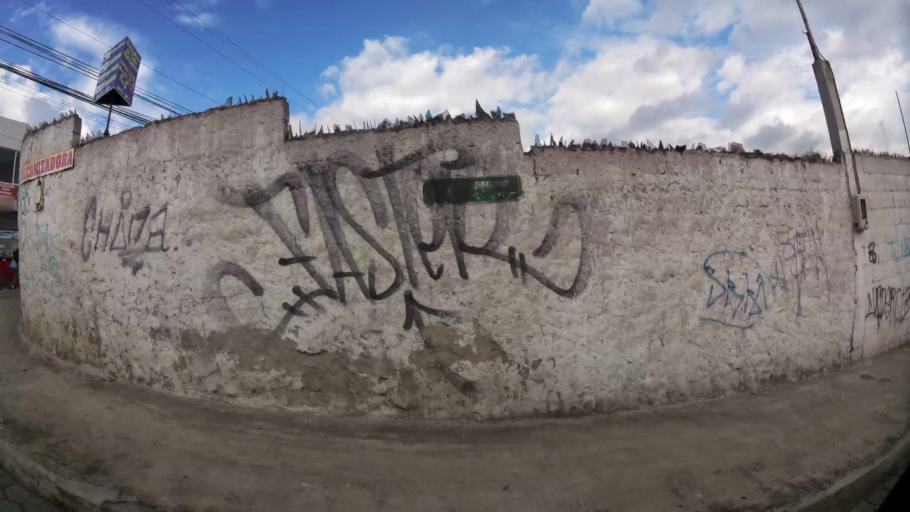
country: EC
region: Pichincha
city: Quito
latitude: -0.1471
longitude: -78.4737
